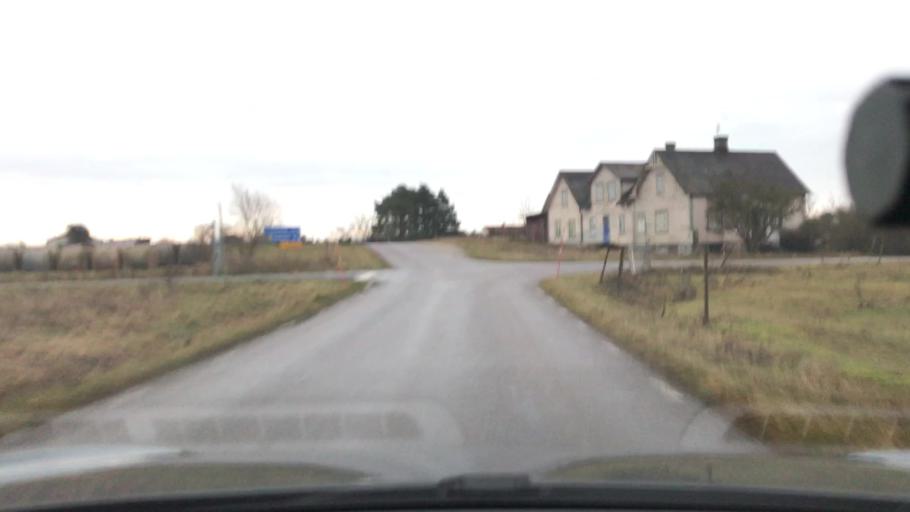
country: SE
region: Gotland
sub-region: Gotland
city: Slite
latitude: 57.3992
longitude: 18.8061
